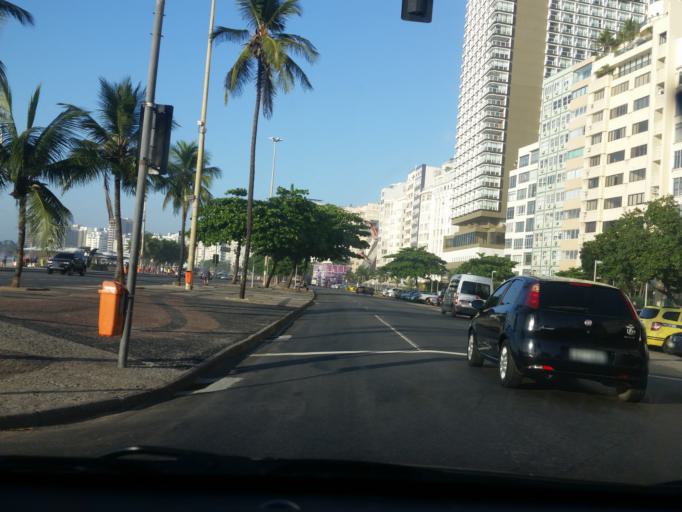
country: BR
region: Rio de Janeiro
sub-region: Rio De Janeiro
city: Rio de Janeiro
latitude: -22.9761
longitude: -43.1880
